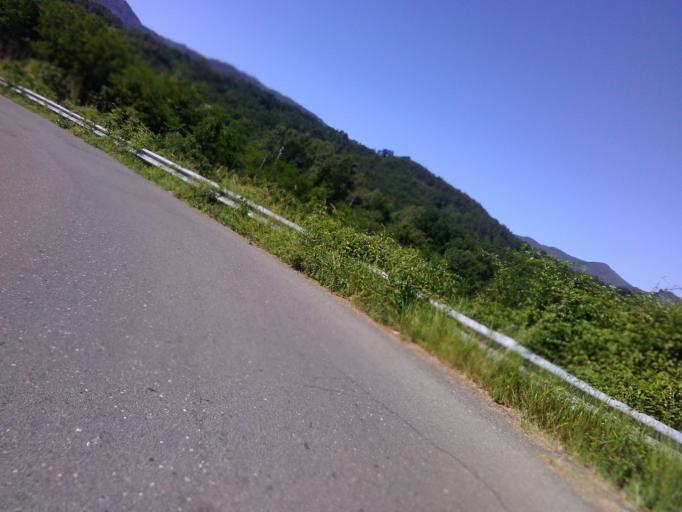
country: IT
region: Tuscany
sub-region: Provincia di Massa-Carrara
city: Pallerone
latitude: 44.1989
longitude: 10.0222
